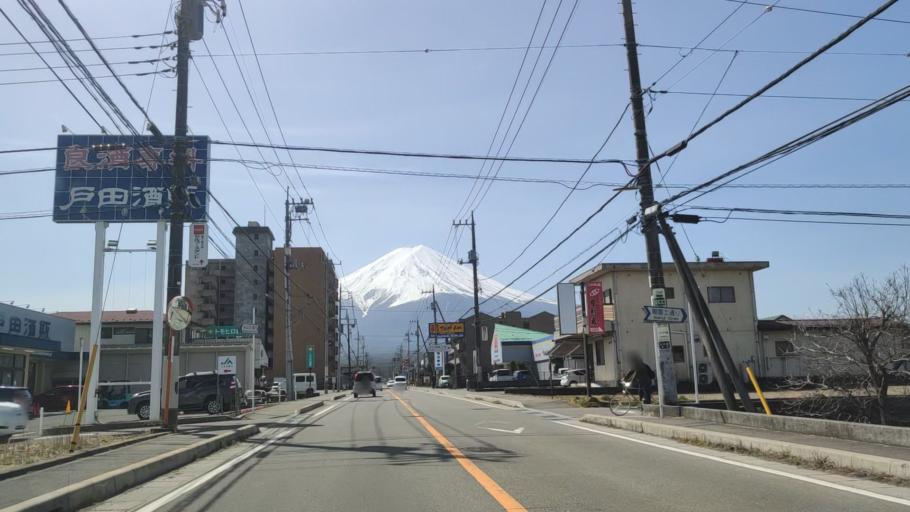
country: JP
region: Yamanashi
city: Fujikawaguchiko
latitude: 35.4960
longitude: 138.7644
